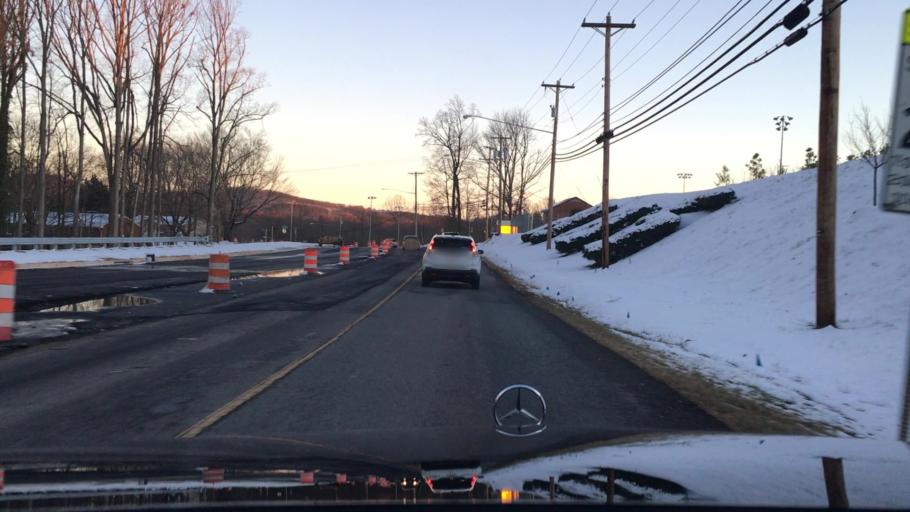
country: US
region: Virginia
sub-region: City of Lynchburg
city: West Lynchburg
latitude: 37.3636
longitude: -79.2049
